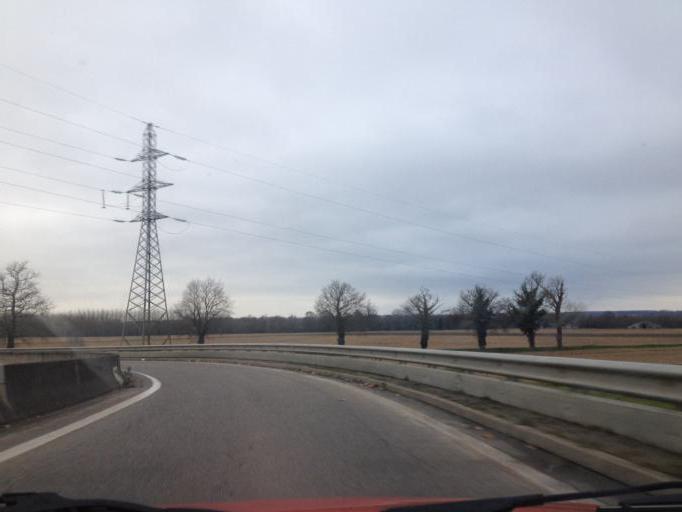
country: FR
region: Auvergne
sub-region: Departement de l'Allier
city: Toulon-sur-Allier
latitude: 46.5292
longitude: 3.3498
